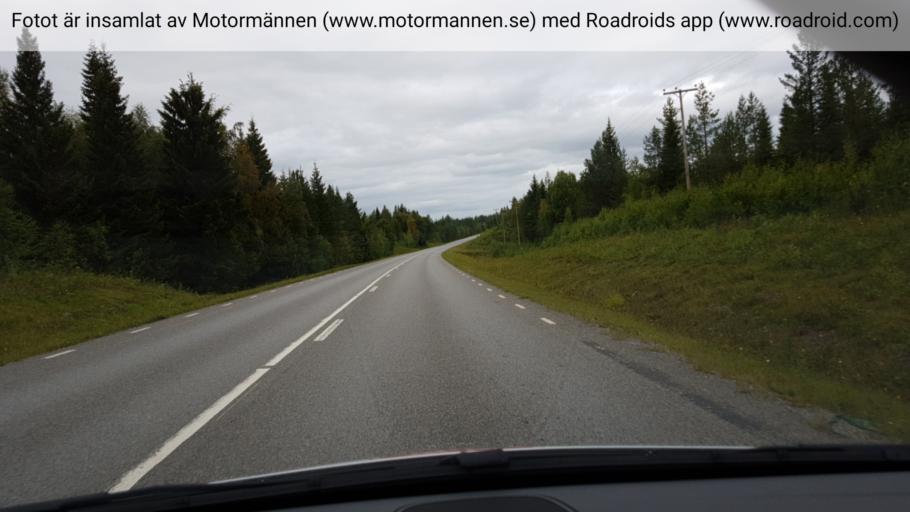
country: SE
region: Jaemtland
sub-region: Stroemsunds Kommun
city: Stroemsund
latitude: 64.2521
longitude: 15.4173
